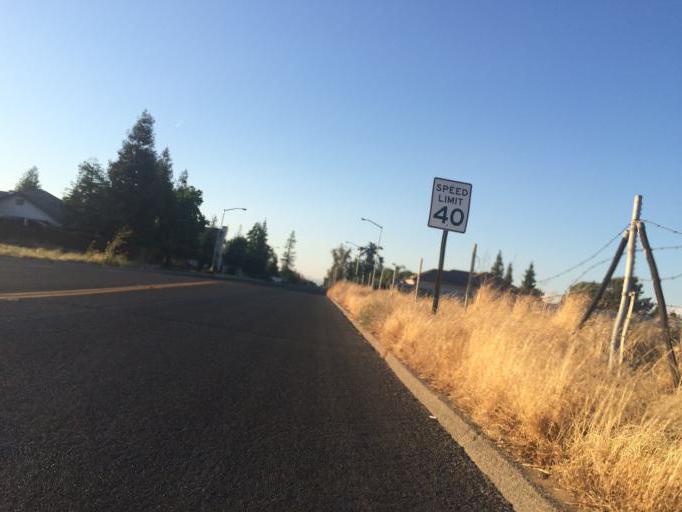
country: US
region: California
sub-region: Fresno County
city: Tarpey Village
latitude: 36.7944
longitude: -119.6730
